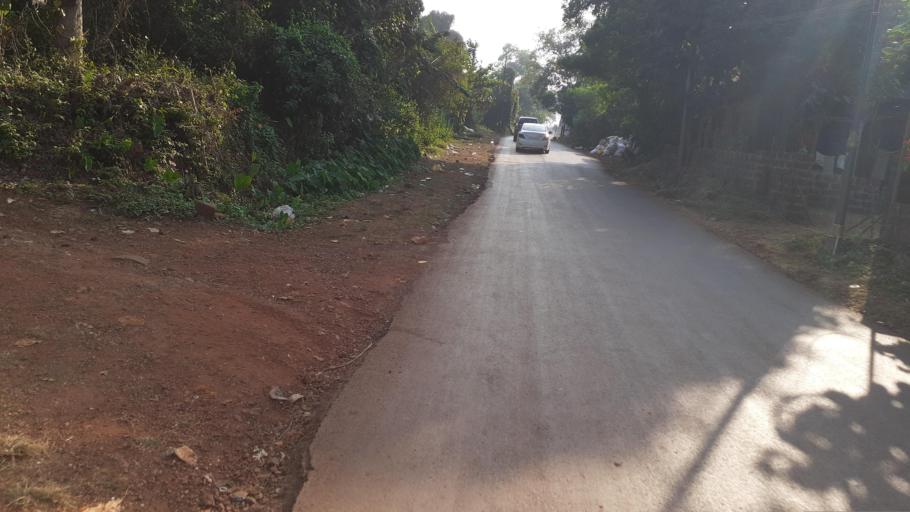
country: IN
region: Maharashtra
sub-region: Ratnagiri
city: Ratnagiri
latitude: 17.1465
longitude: 73.2711
